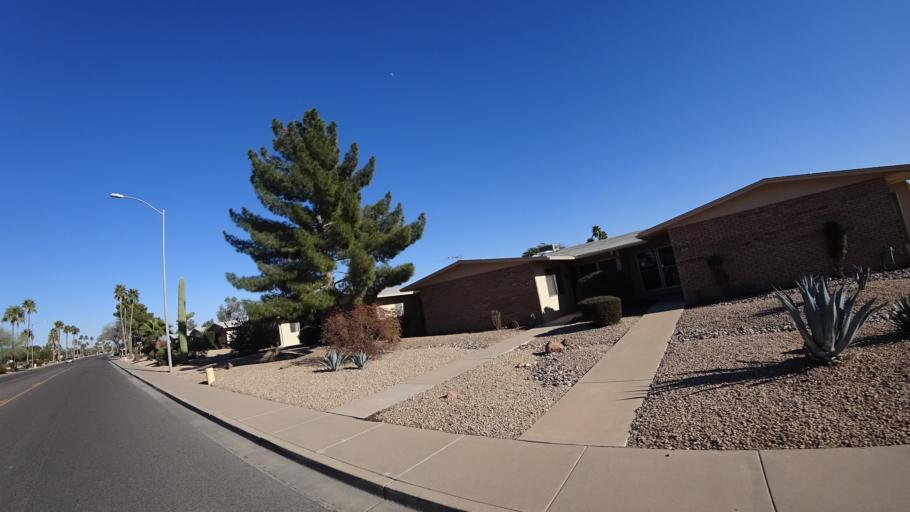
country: US
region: Arizona
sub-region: Maricopa County
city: Sun City West
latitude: 33.6580
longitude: -112.3492
